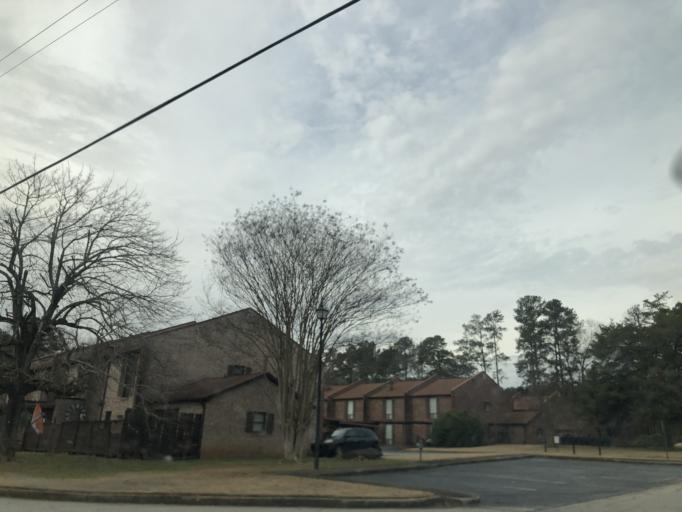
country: US
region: Georgia
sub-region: DeKalb County
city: Pine Mountain
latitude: 33.6397
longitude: -84.1827
